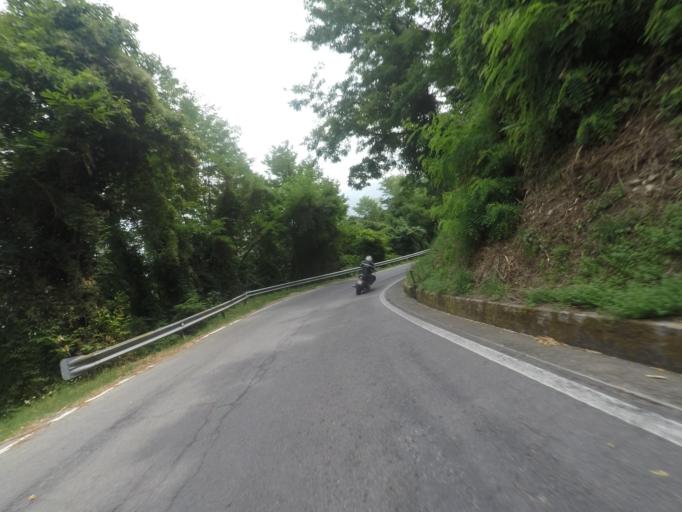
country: IT
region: Tuscany
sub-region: Provincia di Lucca
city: Castelnuovo di Garfagnana
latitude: 44.1094
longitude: 10.4038
